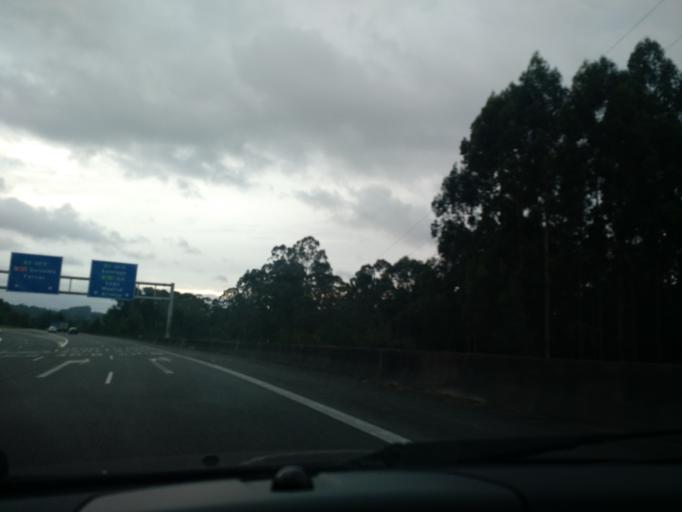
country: ES
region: Galicia
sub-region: Provincia da Coruna
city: Oleiros
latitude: 43.2878
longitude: -8.2897
